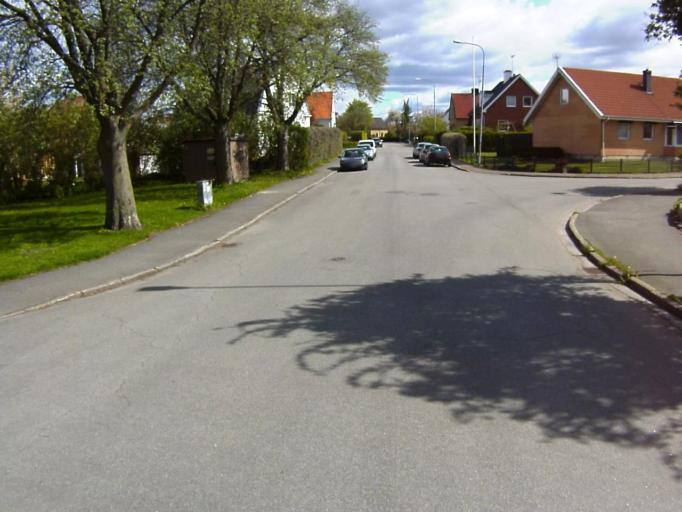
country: SE
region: Skane
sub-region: Kristianstads Kommun
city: Kristianstad
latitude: 56.0369
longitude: 14.1650
